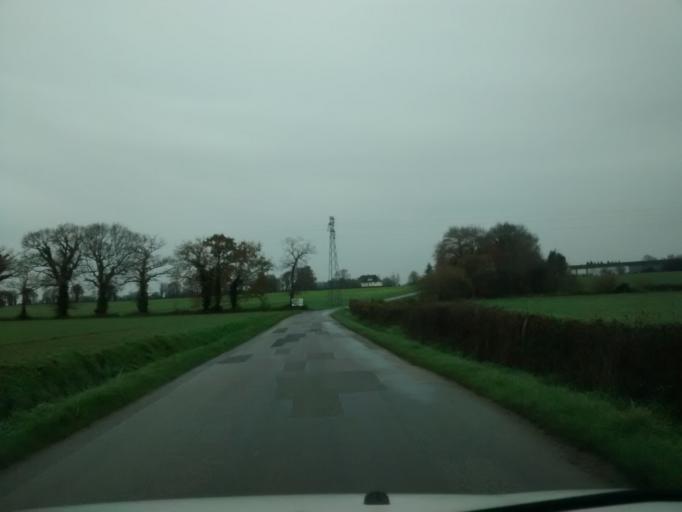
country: FR
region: Brittany
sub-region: Departement d'Ille-et-Vilaine
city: Acigne
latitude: 48.1403
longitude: -1.5473
